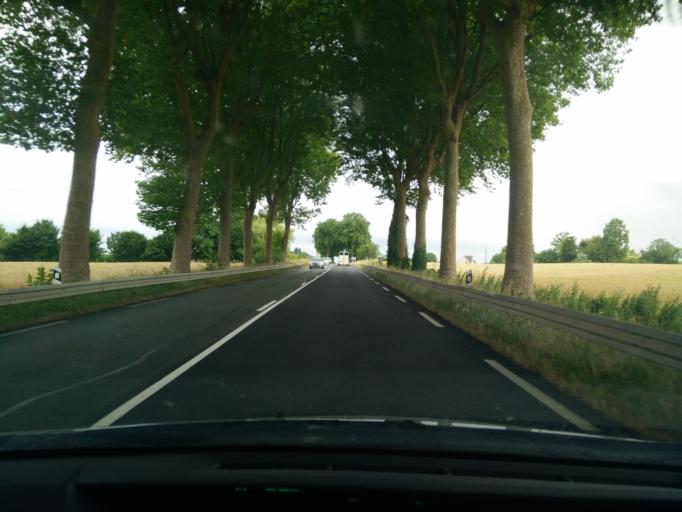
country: FR
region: Pays de la Loire
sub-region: Departement de Maine-et-Loire
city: Brissac-Quince
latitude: 47.3133
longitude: -0.4022
